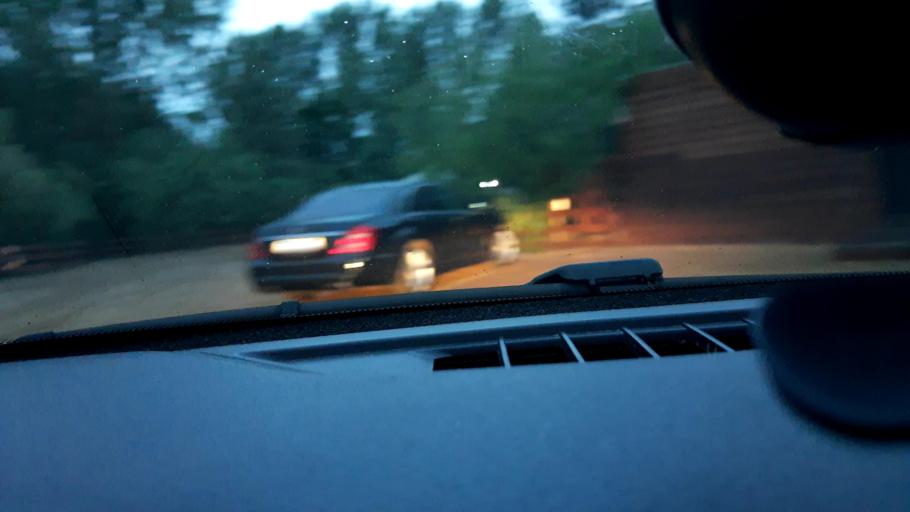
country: RU
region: Nizjnij Novgorod
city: Bor
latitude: 56.3304
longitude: 44.0500
